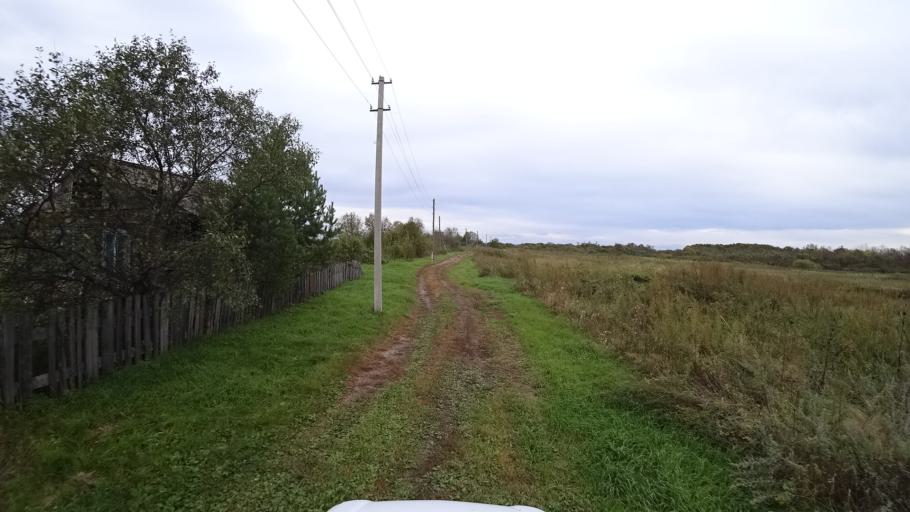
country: RU
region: Amur
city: Arkhara
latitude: 49.4320
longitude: 130.2573
